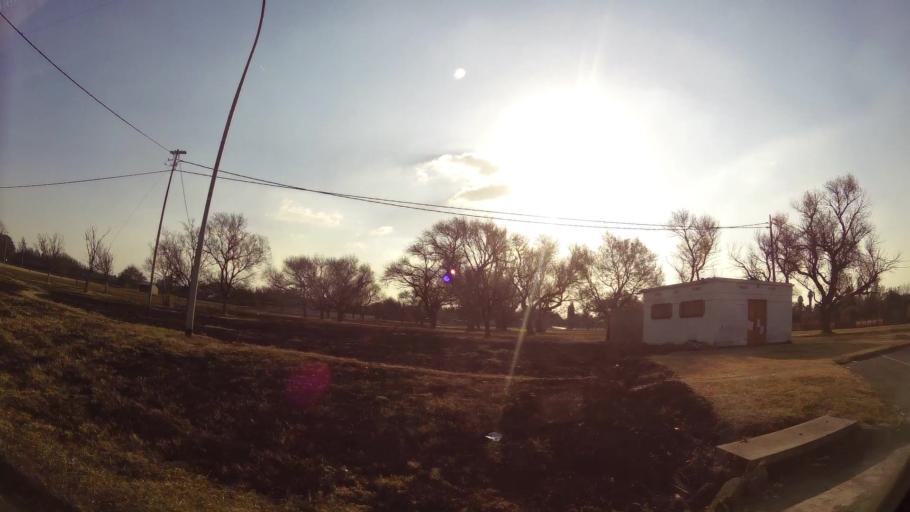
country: ZA
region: Gauteng
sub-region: Ekurhuleni Metropolitan Municipality
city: Brakpan
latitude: -26.2547
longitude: 28.3775
